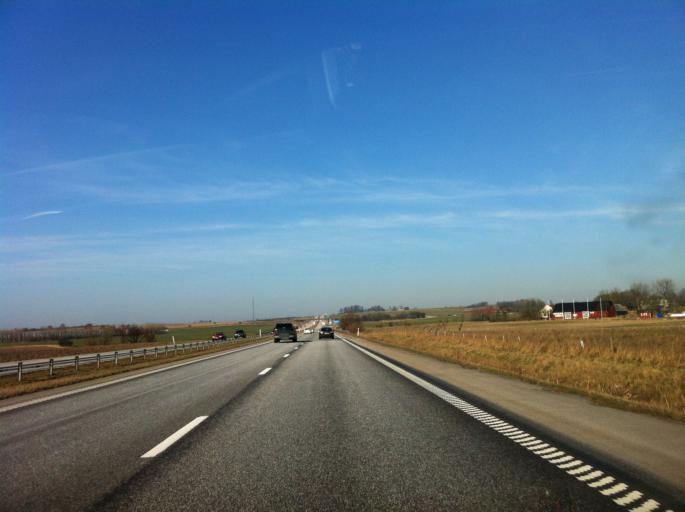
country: SE
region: Skane
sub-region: Helsingborg
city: Glumslov
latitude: 55.9181
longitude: 12.8471
